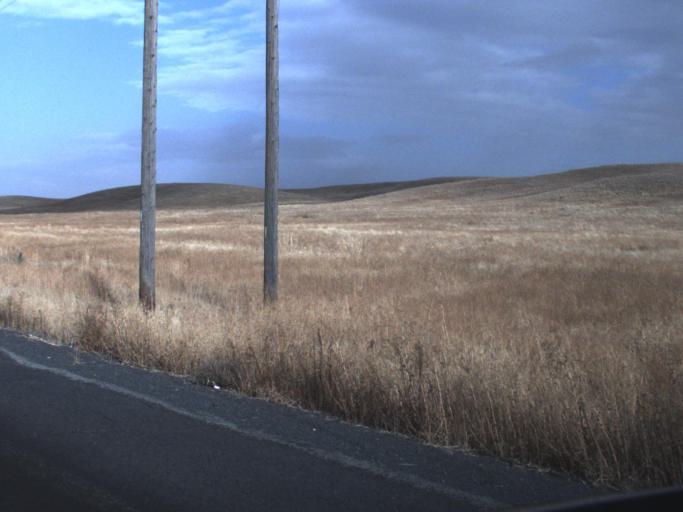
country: US
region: Washington
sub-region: Lincoln County
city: Davenport
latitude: 47.5372
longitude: -118.1970
